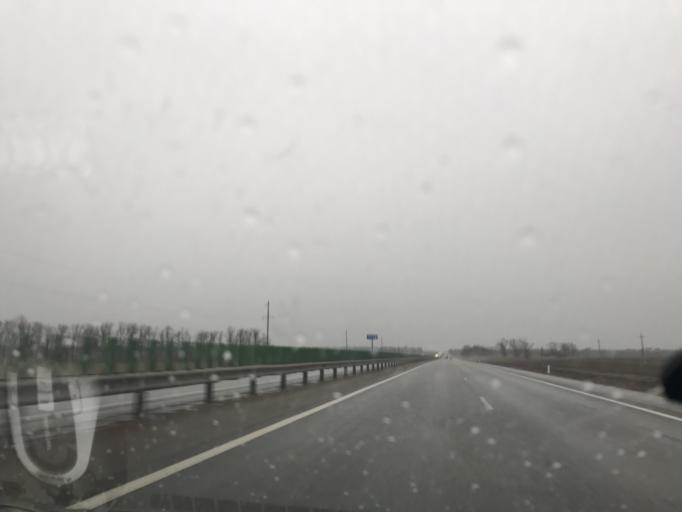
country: RU
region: Krasnodarskiy
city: Kislyakovskaya
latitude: 46.3336
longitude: 39.7865
